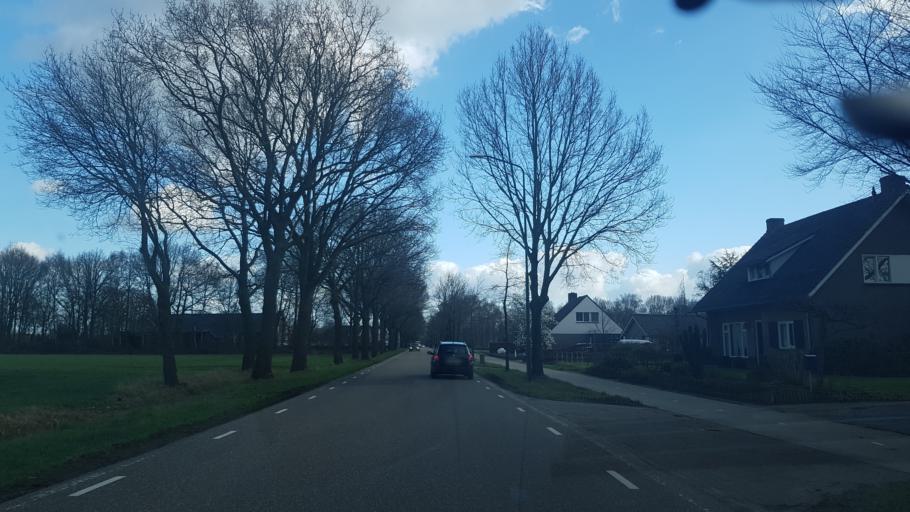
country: NL
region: North Brabant
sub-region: Gemeente Eersel
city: Eersel
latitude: 51.3806
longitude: 5.2974
